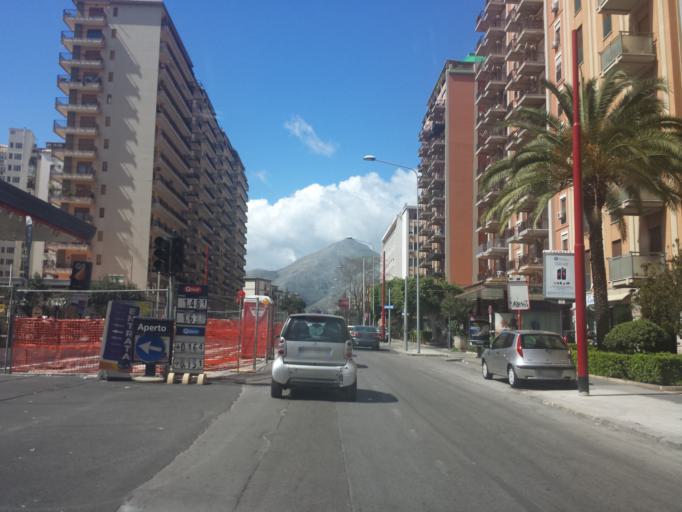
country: IT
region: Sicily
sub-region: Palermo
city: Palermo
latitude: 38.1298
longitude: 13.3342
